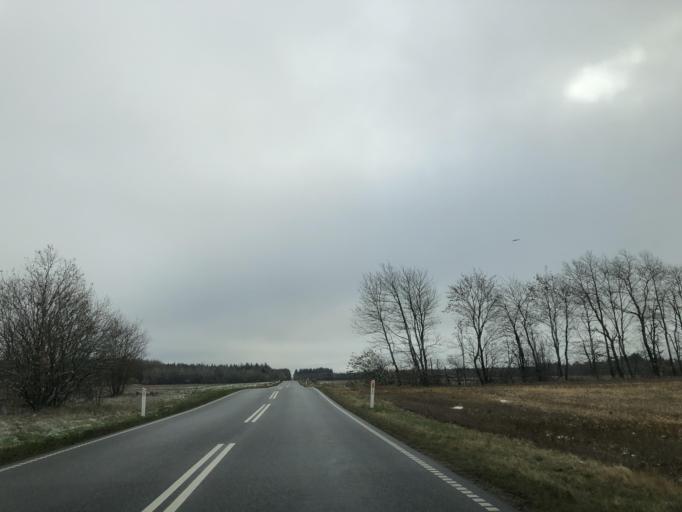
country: DK
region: Central Jutland
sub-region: Ikast-Brande Kommune
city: Brande
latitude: 55.9884
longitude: 9.2222
